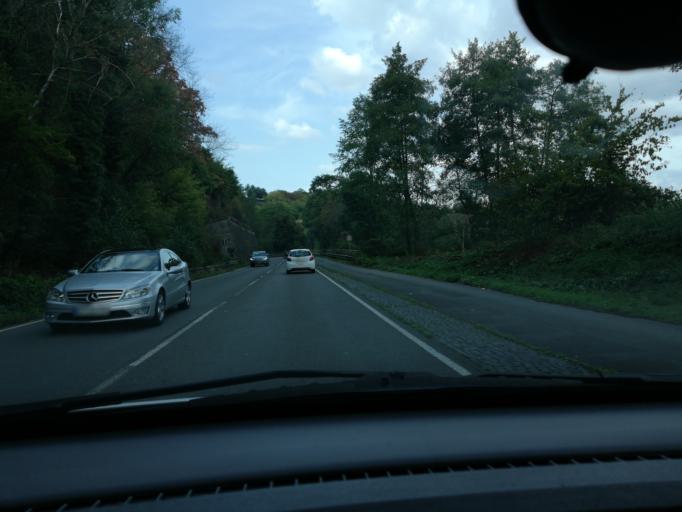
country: DE
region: North Rhine-Westphalia
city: Witten
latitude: 51.4277
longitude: 7.3014
